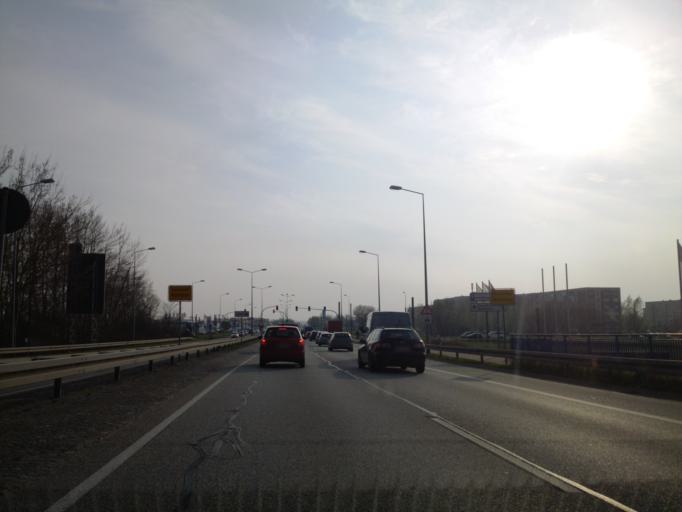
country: DE
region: Mecklenburg-Vorpommern
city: Dierkow-Neu
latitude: 54.1033
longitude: 12.1827
